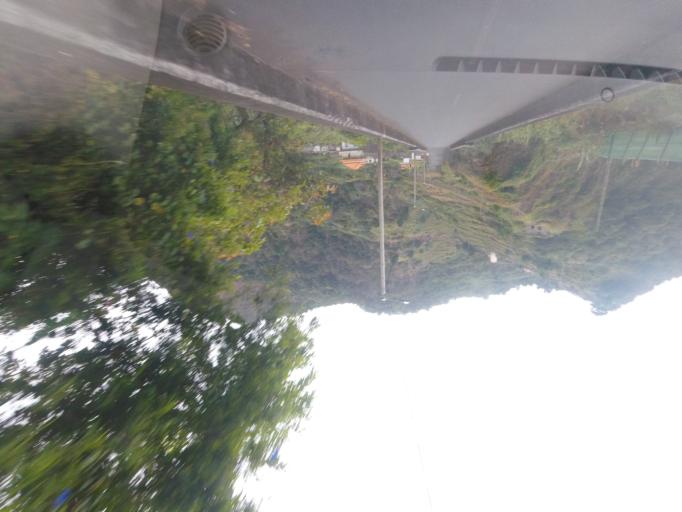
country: PT
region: Madeira
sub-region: Santana
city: Santana
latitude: 32.8175
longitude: -16.8985
